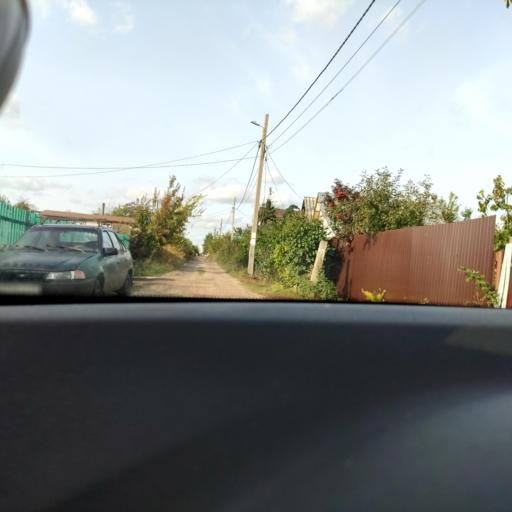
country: RU
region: Samara
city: Petra-Dubrava
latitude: 53.2815
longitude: 50.2956
